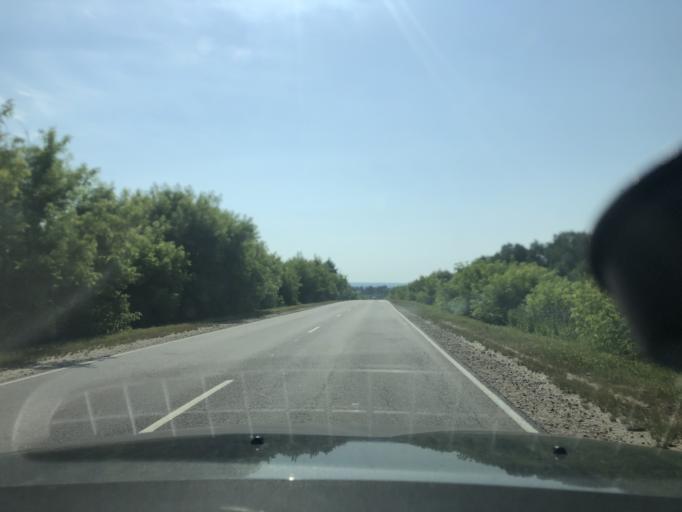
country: RU
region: Tula
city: Dubna
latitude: 54.1123
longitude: 37.0947
